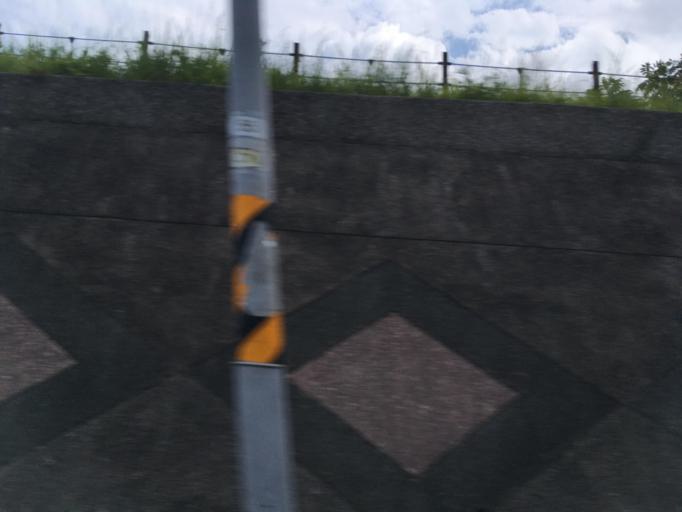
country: TW
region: Taiwan
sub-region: Yilan
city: Yilan
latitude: 24.4431
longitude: 121.7769
